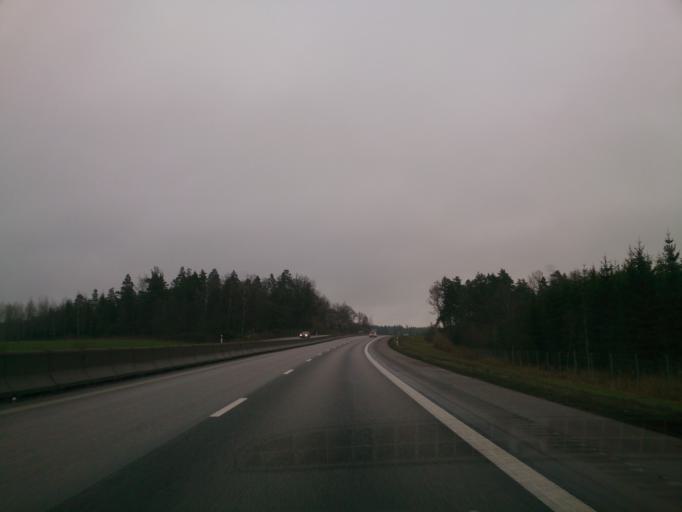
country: SE
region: OEstergoetland
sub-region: Norrkopings Kommun
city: Kimstad
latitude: 58.5282
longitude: 16.0177
